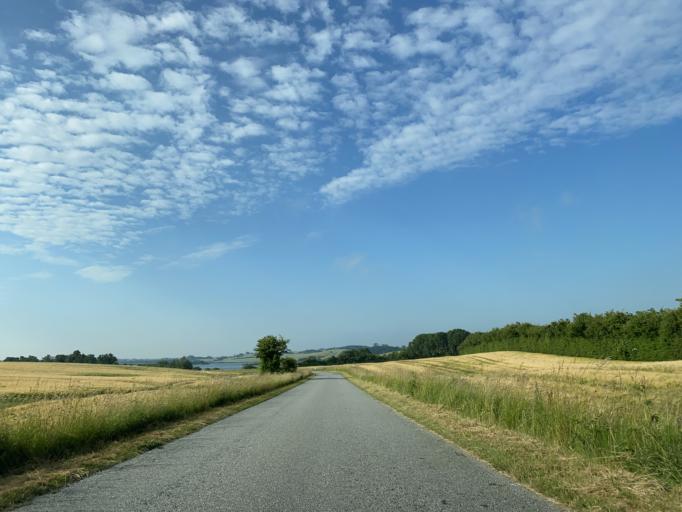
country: DK
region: South Denmark
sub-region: Haderslev Kommune
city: Haderslev
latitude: 55.1767
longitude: 9.4813
